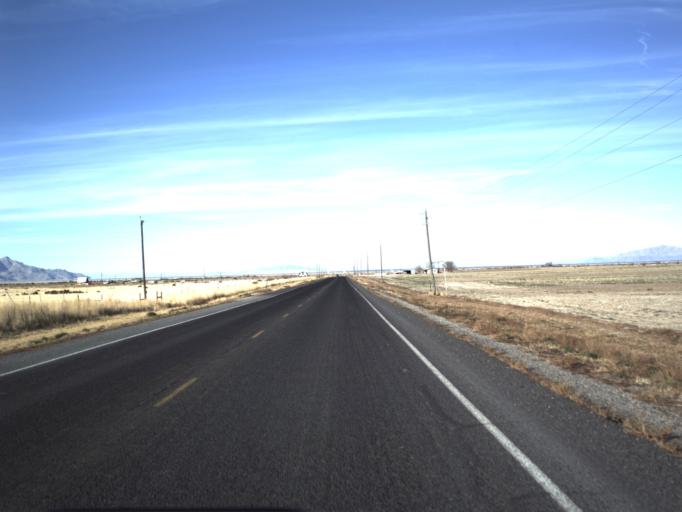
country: US
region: Utah
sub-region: Tooele County
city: Erda
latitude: 40.6035
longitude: -112.3707
